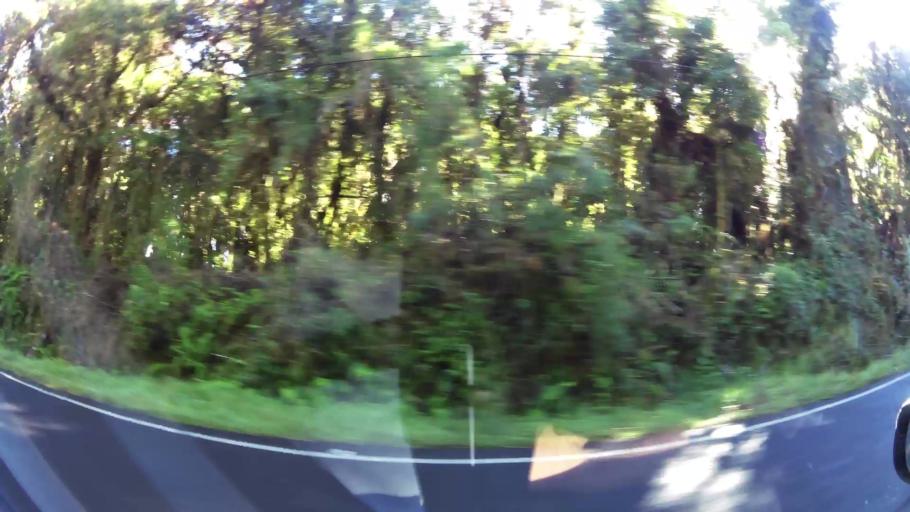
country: CR
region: San Jose
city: San Marcos
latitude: 9.7066
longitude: -83.9471
